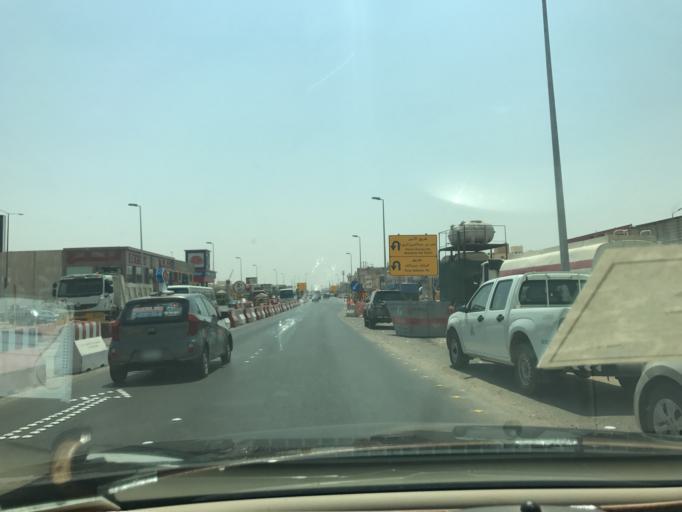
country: SA
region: Ar Riyad
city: Riyadh
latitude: 24.7508
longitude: 46.7718
